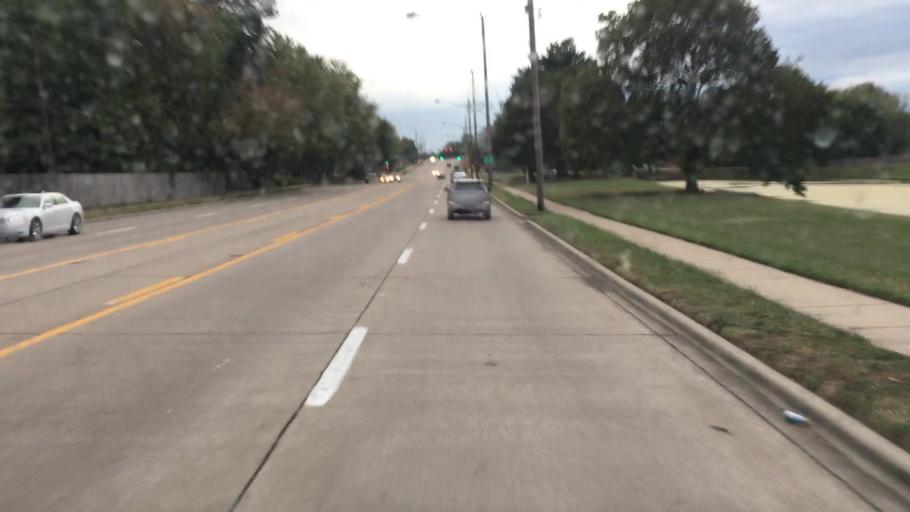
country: US
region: Missouri
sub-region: Saint Louis County
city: Florissant
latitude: 38.8229
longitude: -90.3387
